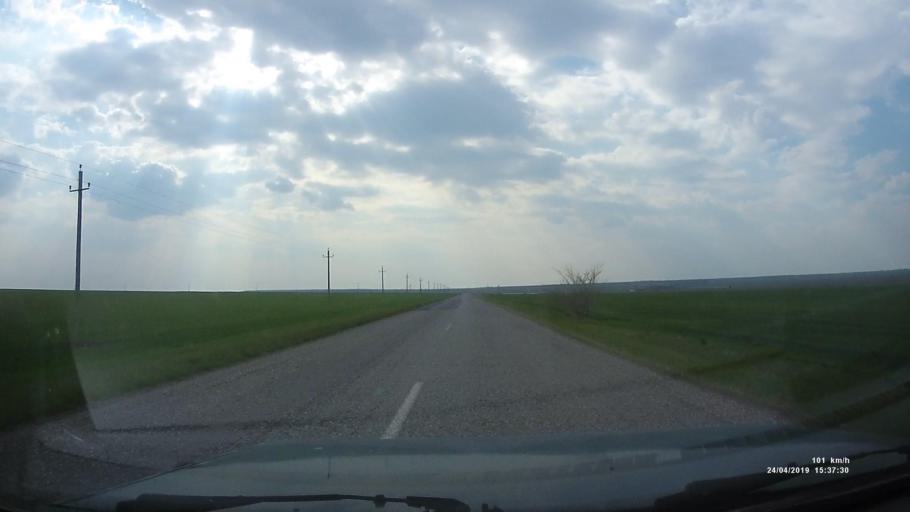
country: RU
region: Kalmykiya
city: Yashalta
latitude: 46.5998
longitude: 42.8477
